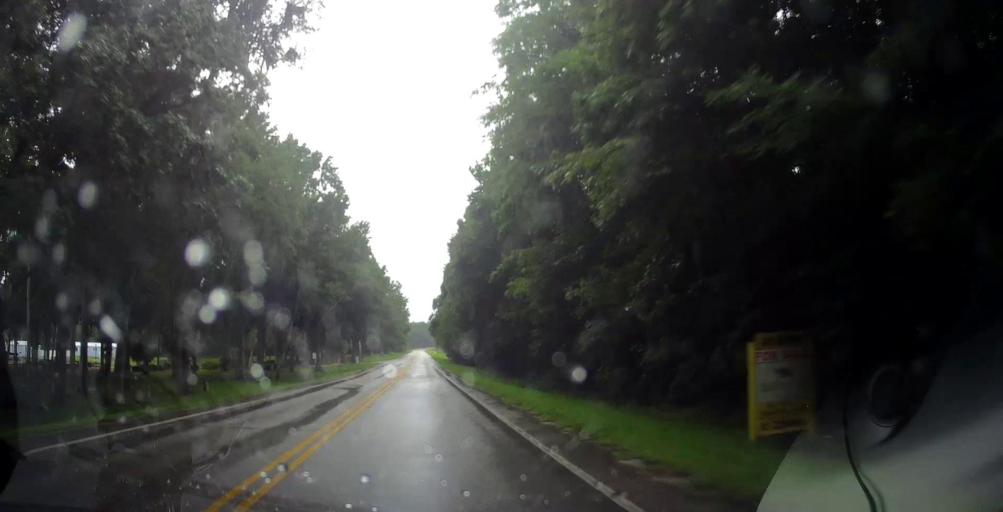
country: US
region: Florida
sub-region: Marion County
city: Citra
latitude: 29.3944
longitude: -82.2474
